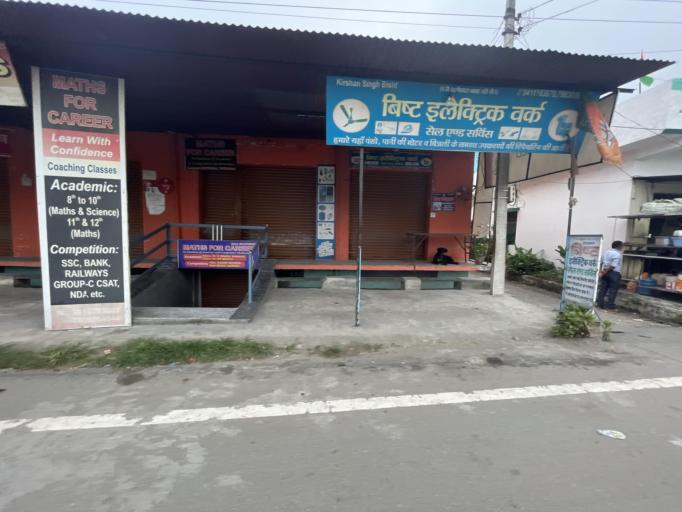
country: IN
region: Uttarakhand
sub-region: Naini Tal
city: Haldwani
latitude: 29.1943
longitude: 79.5038
